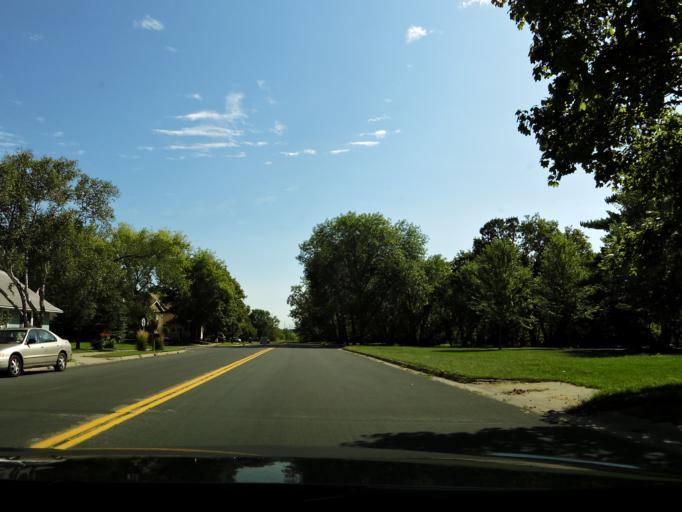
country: US
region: Minnesota
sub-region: Carver County
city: Chanhassen
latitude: 44.8621
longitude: -93.5286
